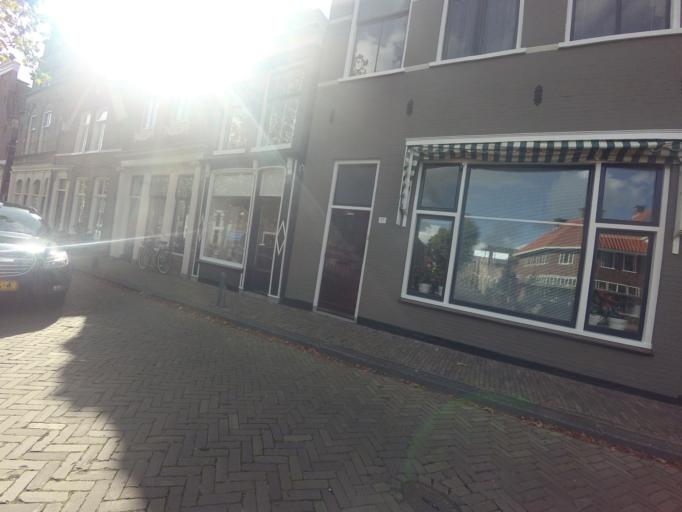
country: NL
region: Friesland
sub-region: Sudwest Fryslan
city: Bolsward
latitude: 53.0635
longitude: 5.5235
